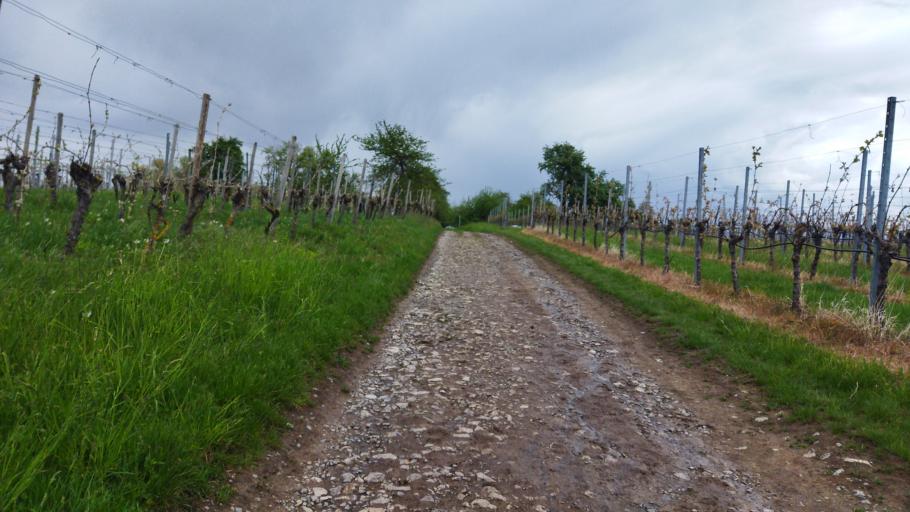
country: DE
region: Baden-Wuerttemberg
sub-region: Regierungsbezirk Stuttgart
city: Hessigheim
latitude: 49.0041
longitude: 9.1925
